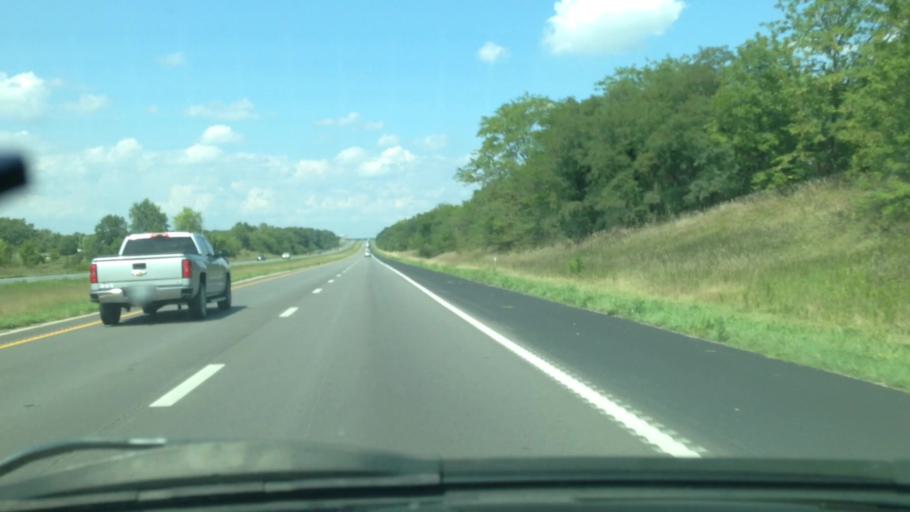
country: US
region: Missouri
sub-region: Lincoln County
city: Troy
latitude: 39.0501
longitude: -90.9739
